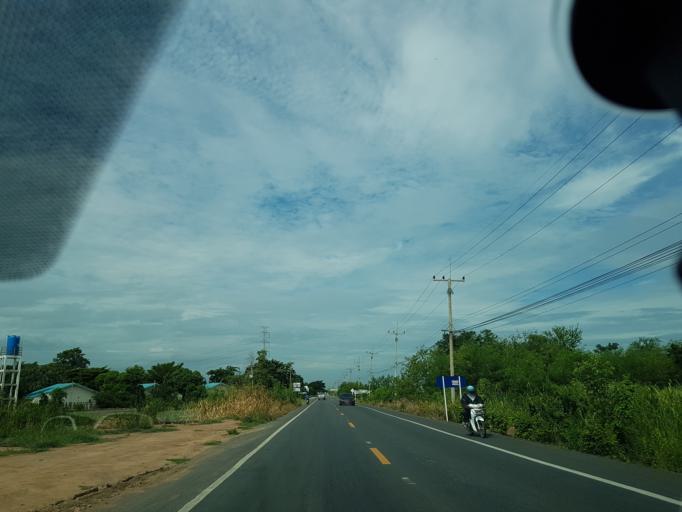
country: TH
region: Lop Buri
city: Tha Wung
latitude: 14.7574
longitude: 100.5593
